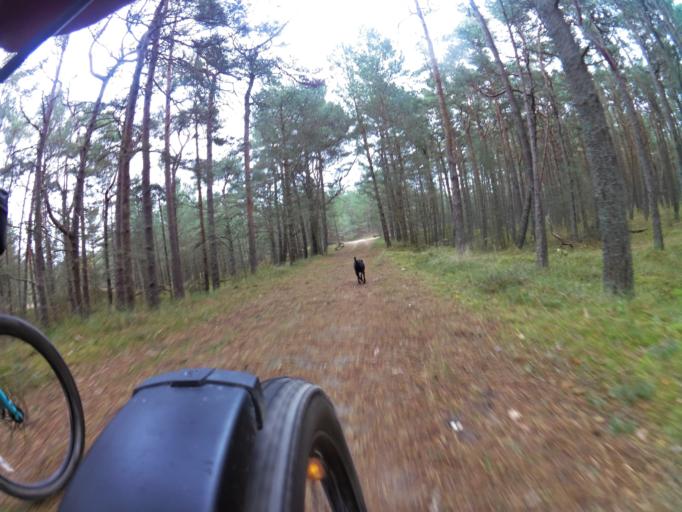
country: PL
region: Pomeranian Voivodeship
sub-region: Powiat leborski
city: Leba
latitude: 54.7698
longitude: 17.5973
